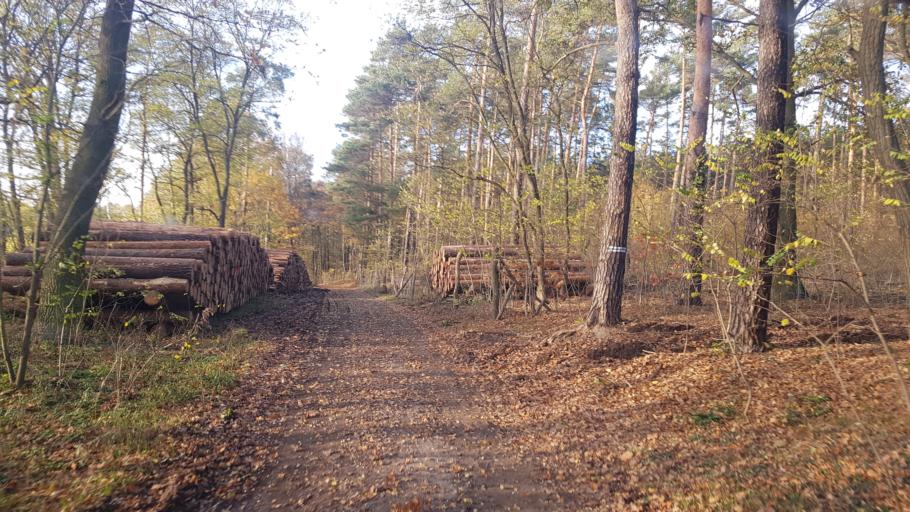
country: DE
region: Brandenburg
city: Calau
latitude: 51.6934
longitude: 13.9645
